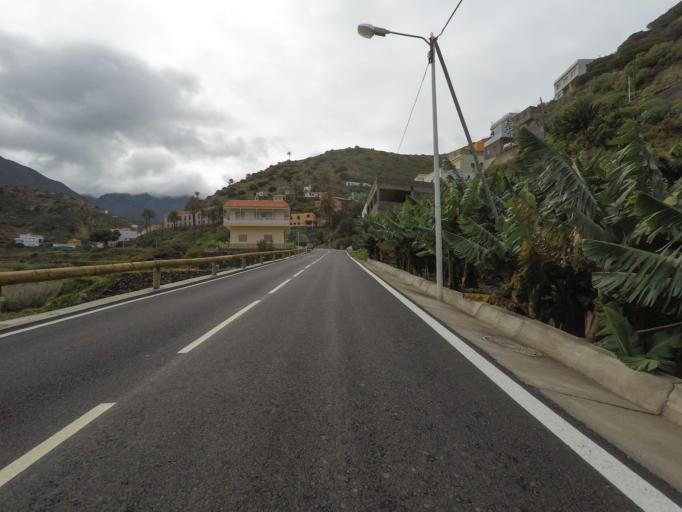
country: ES
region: Canary Islands
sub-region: Provincia de Santa Cruz de Tenerife
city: Vallehermosa
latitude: 28.1854
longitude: -17.2643
